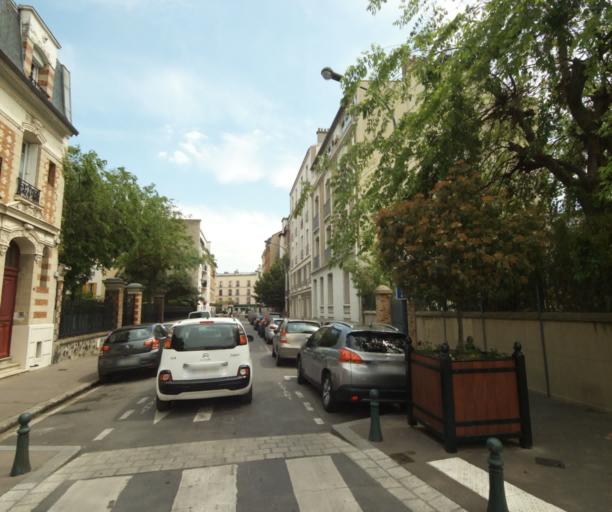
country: FR
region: Ile-de-France
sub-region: Departement des Hauts-de-Seine
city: Asnieres-sur-Seine
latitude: 48.9128
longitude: 2.2940
